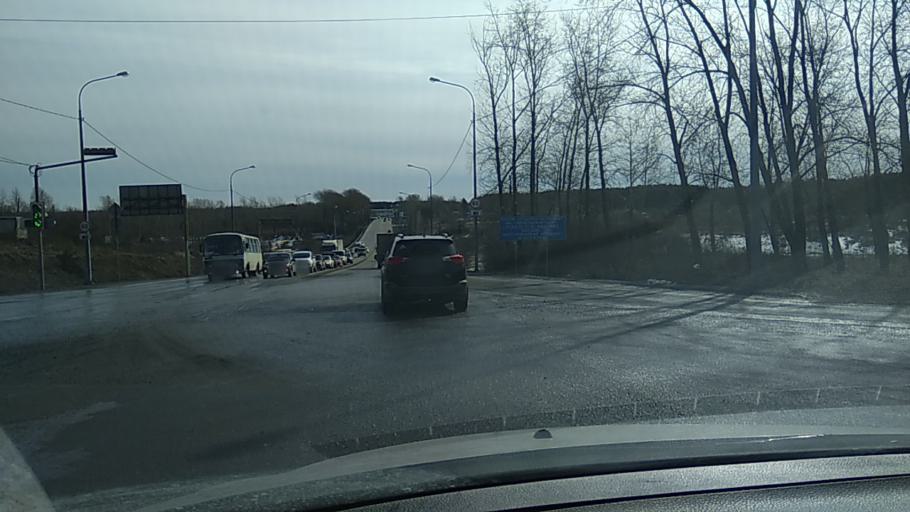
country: RU
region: Sverdlovsk
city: Nizhniy Tagil
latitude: 57.8855
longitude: 60.0166
